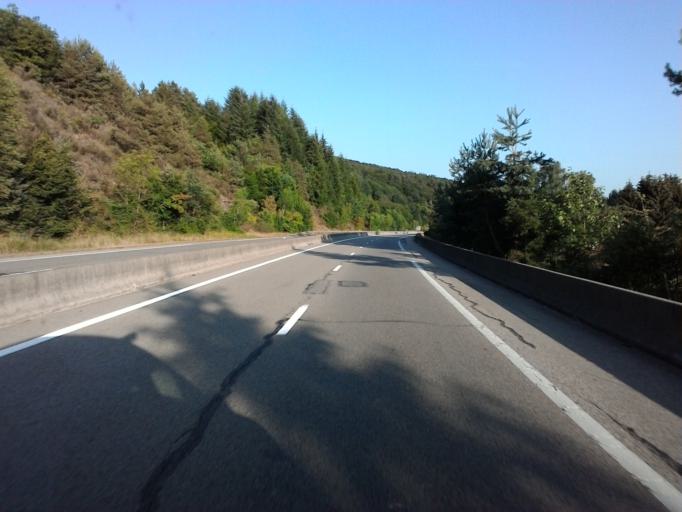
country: FR
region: Lorraine
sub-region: Departement des Vosges
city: Arches
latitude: 48.1453
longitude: 6.5075
